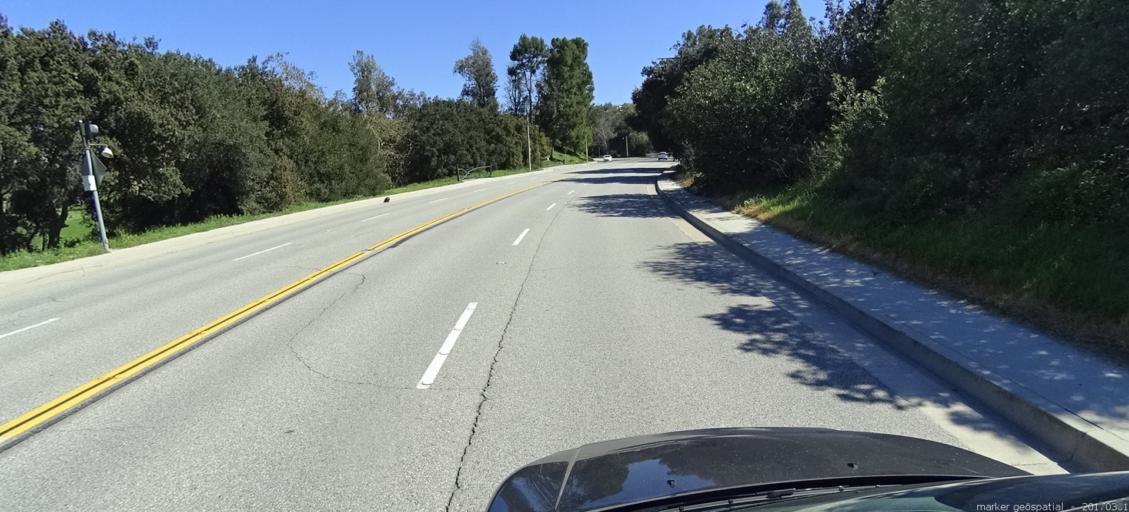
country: US
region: California
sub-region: Orange County
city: Villa Park
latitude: 33.8408
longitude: -117.7713
